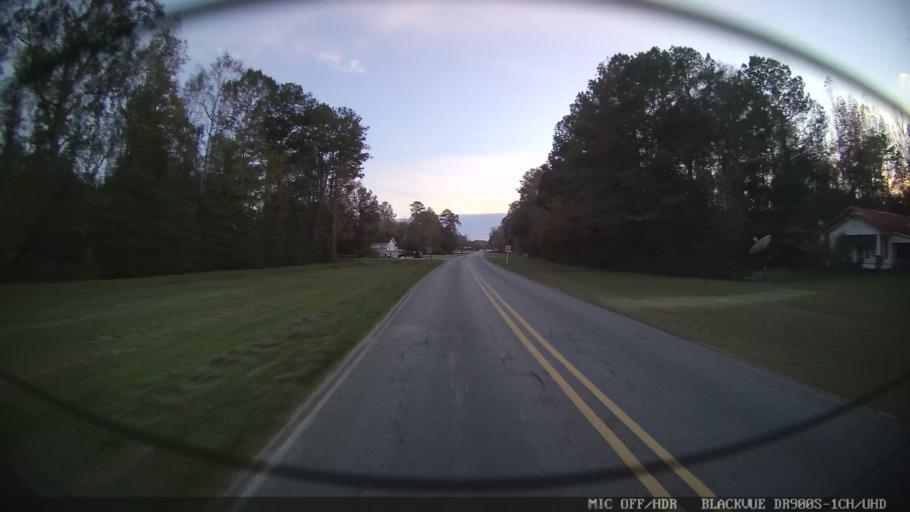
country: US
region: Mississippi
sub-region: Perry County
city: New Augusta
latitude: 31.0608
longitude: -89.1899
